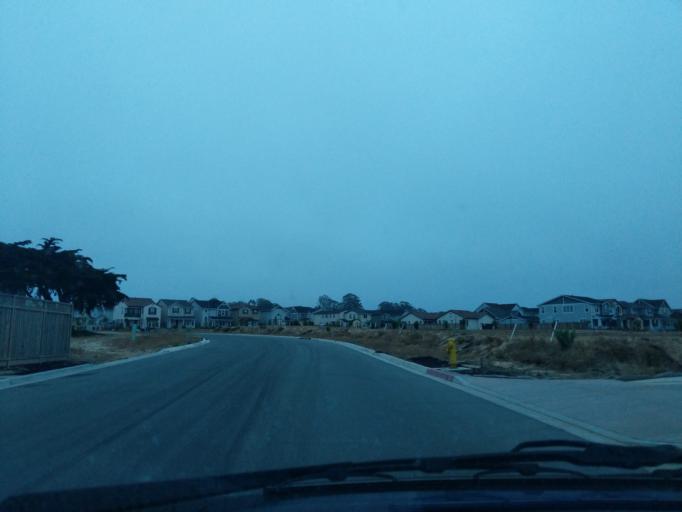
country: US
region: California
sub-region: Monterey County
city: Boronda
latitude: 36.6543
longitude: -121.7333
